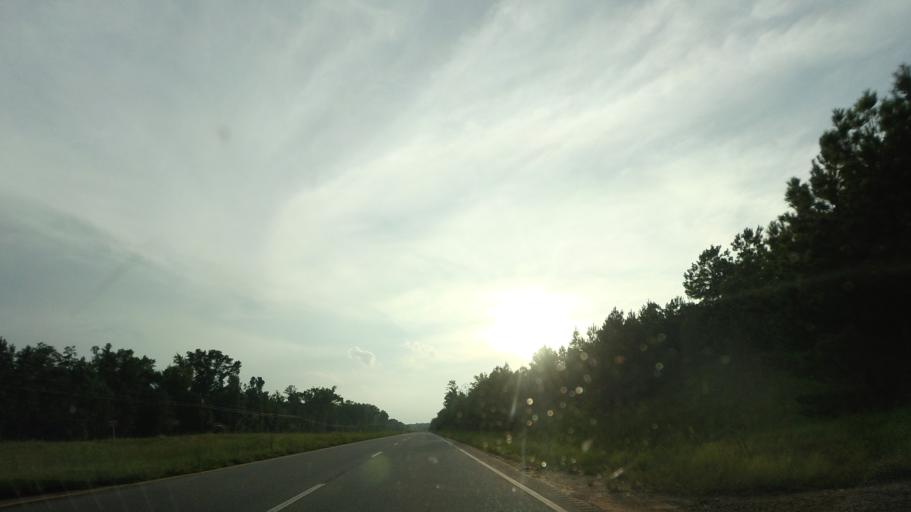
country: US
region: Georgia
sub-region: Wilkinson County
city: Gordon
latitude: 32.8512
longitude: -83.4085
